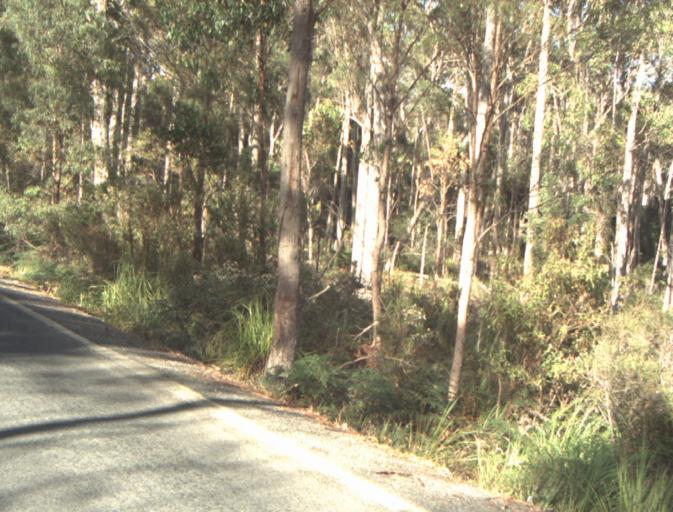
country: AU
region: Tasmania
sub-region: Dorset
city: Bridport
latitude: -41.1563
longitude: 147.2381
